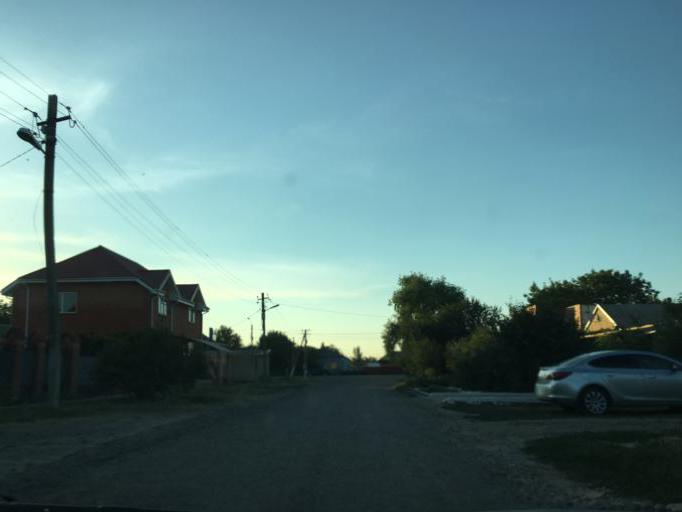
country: RU
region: Krasnodarskiy
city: Kushchevskaya
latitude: 46.5680
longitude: 39.6484
